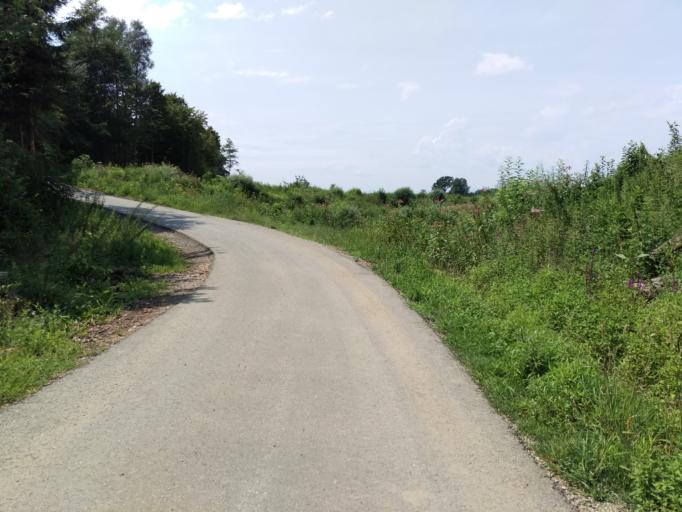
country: AT
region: Styria
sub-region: Politischer Bezirk Graz-Umgebung
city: Hart bei Graz
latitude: 47.0399
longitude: 15.5132
